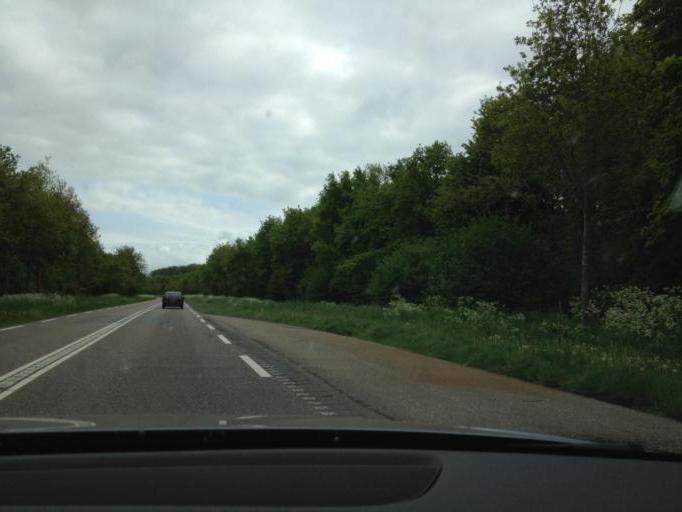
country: NL
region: North Holland
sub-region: Gemeente Huizen
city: Huizen
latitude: 52.3473
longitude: 5.2614
